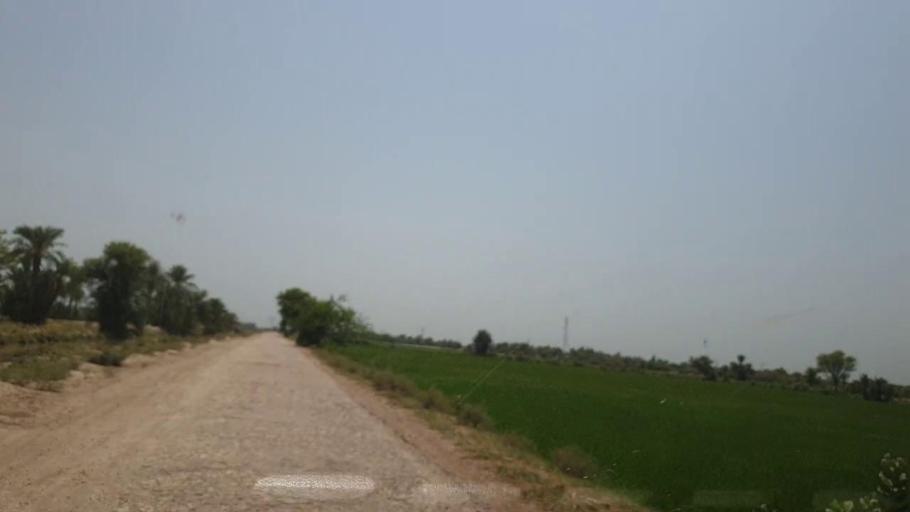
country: PK
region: Sindh
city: Lakhi
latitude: 27.8664
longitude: 68.6069
